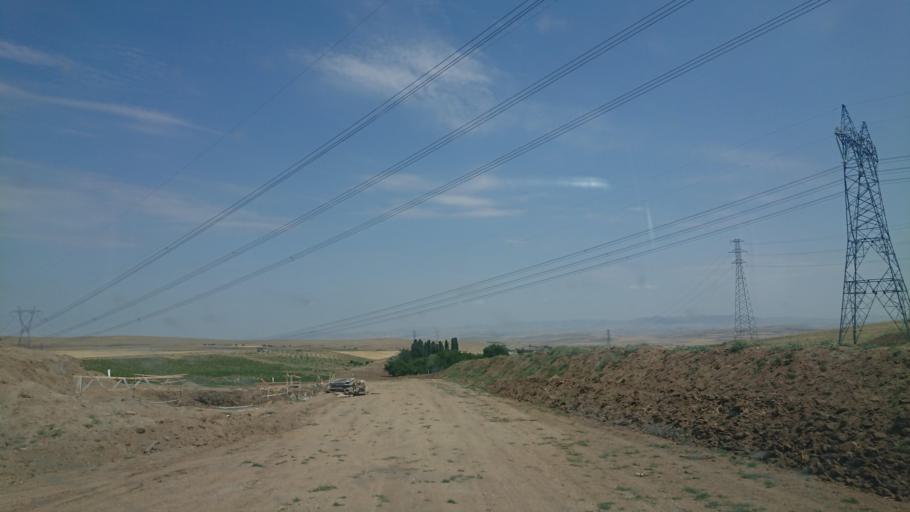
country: TR
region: Aksaray
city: Agacoren
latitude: 38.9016
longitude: 33.9242
